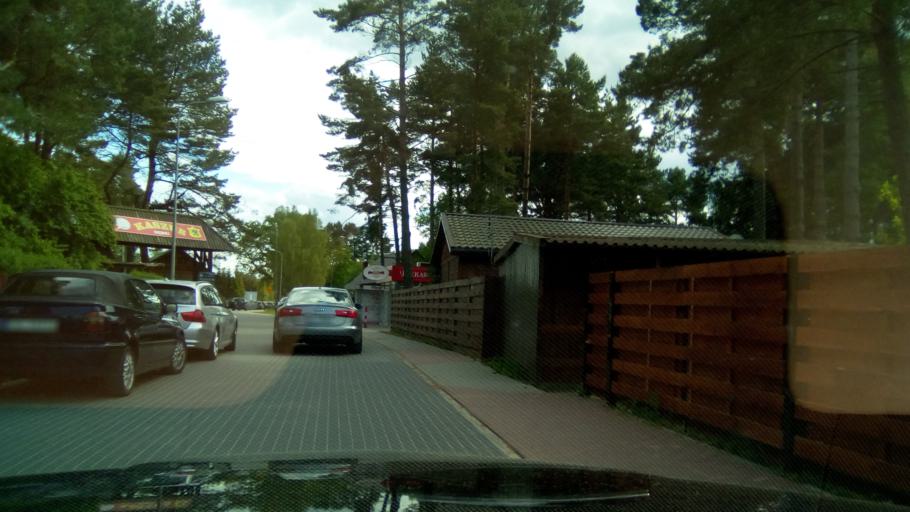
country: PL
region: Pomeranian Voivodeship
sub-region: Powiat pucki
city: Wierzchucino
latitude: 54.8295
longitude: 18.0762
